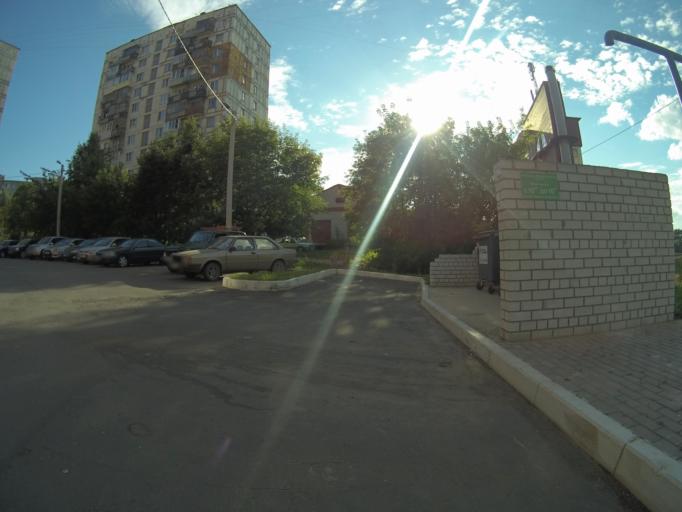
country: RU
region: Vladimir
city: Vladimir
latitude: 56.1528
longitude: 40.3703
